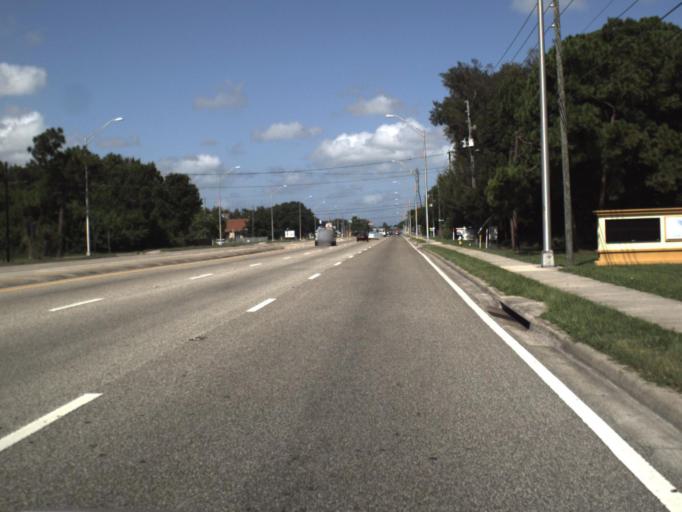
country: US
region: Florida
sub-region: Pinellas County
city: South Highpoint
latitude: 27.9163
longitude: -82.7144
